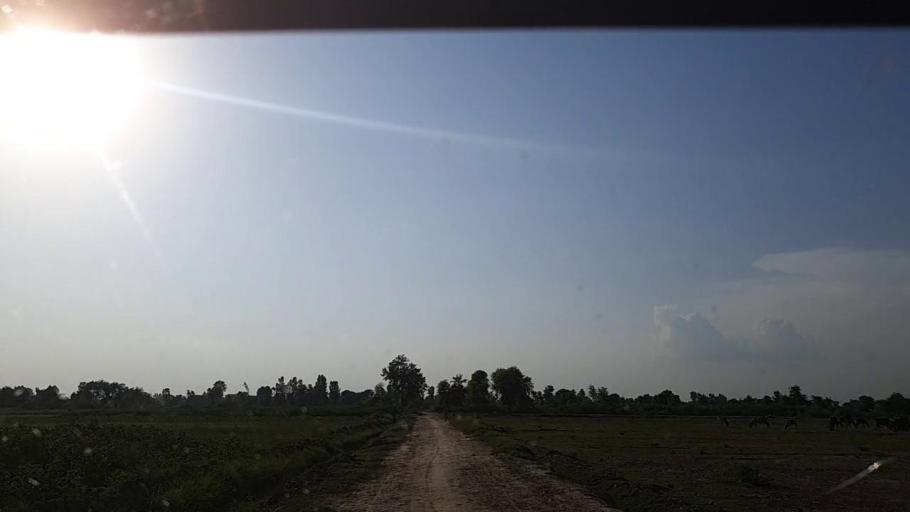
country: PK
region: Sindh
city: Pano Aqil
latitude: 27.9071
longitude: 69.2044
